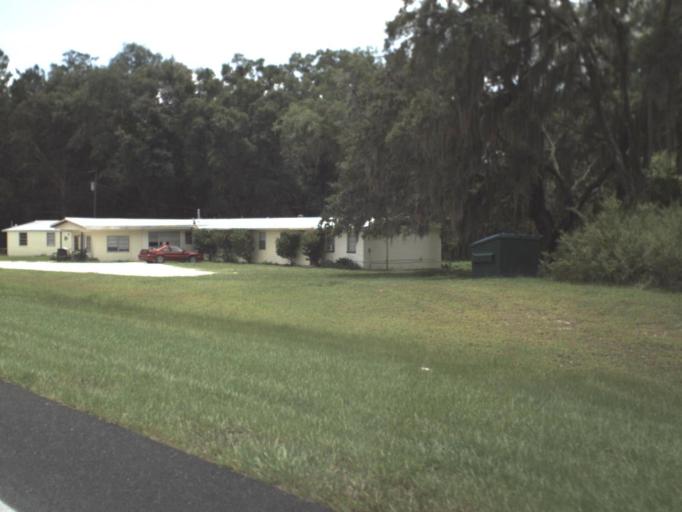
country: US
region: Florida
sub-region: Levy County
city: Williston
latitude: 29.3925
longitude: -82.4788
